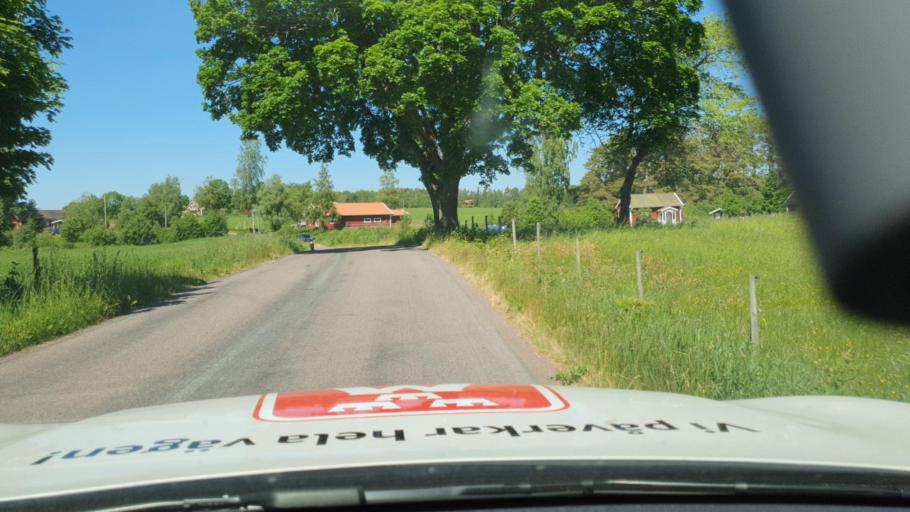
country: SE
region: Joenkoeping
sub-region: Habo Kommun
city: Habo
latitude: 57.9601
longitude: 14.0679
